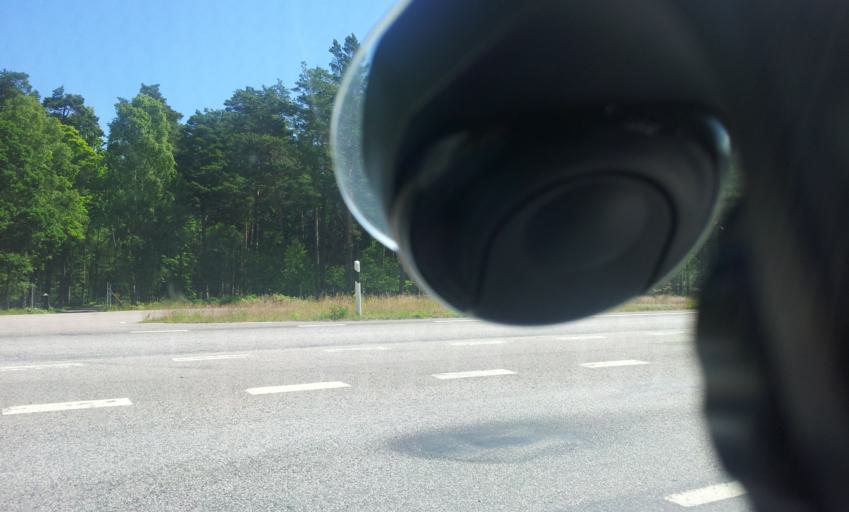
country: SE
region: Kalmar
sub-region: Oskarshamns Kommun
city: Paskallavik
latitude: 57.1245
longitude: 16.4874
